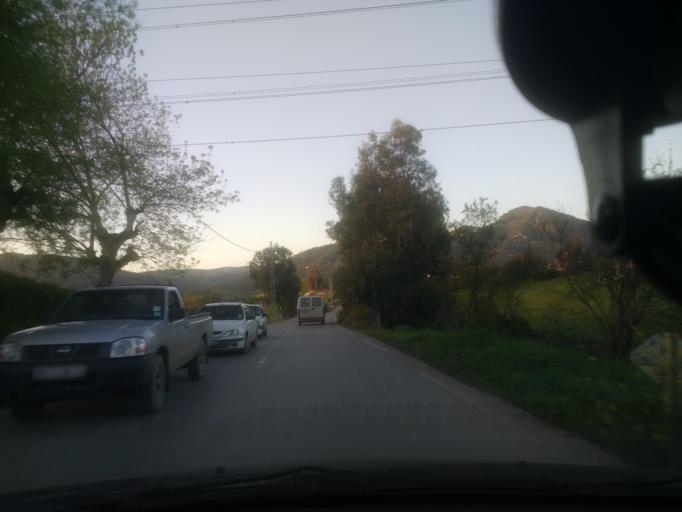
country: DZ
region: Boumerdes
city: Makouda
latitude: 36.7614
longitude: 4.0646
